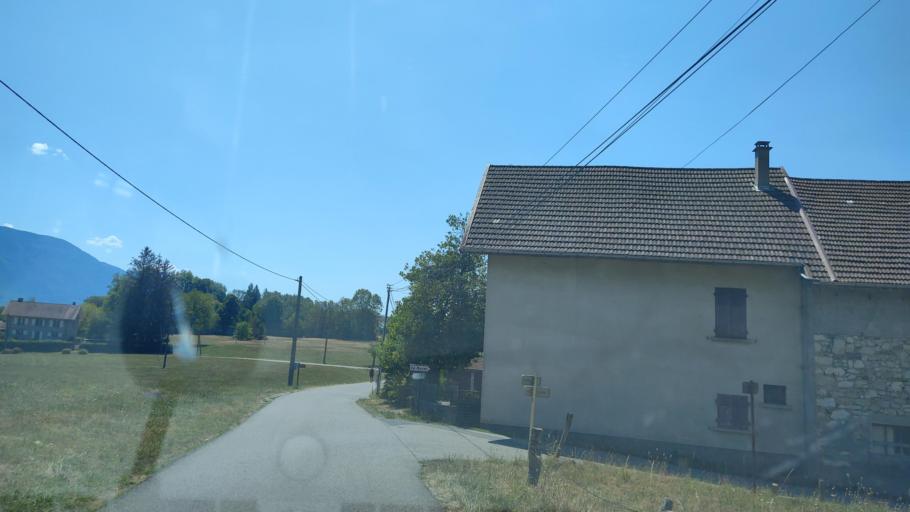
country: FR
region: Rhone-Alpes
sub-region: Departement de la Savoie
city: Novalaise
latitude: 45.5920
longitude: 5.7901
